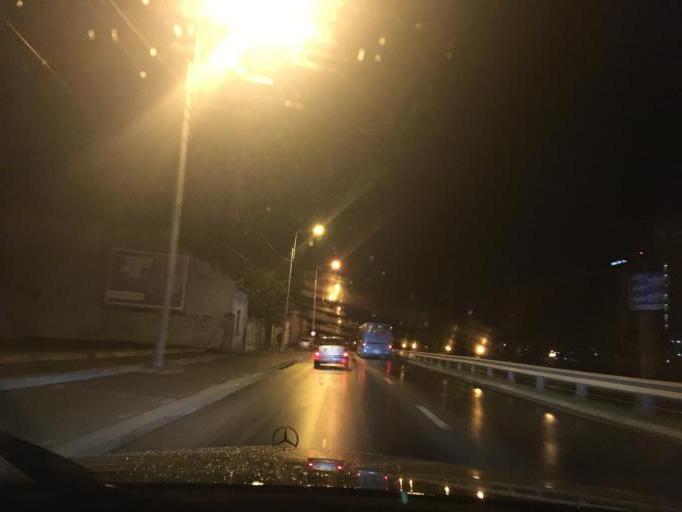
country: RO
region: Bihor
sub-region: Comuna Biharea
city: Oradea
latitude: 47.0519
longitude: 21.9506
